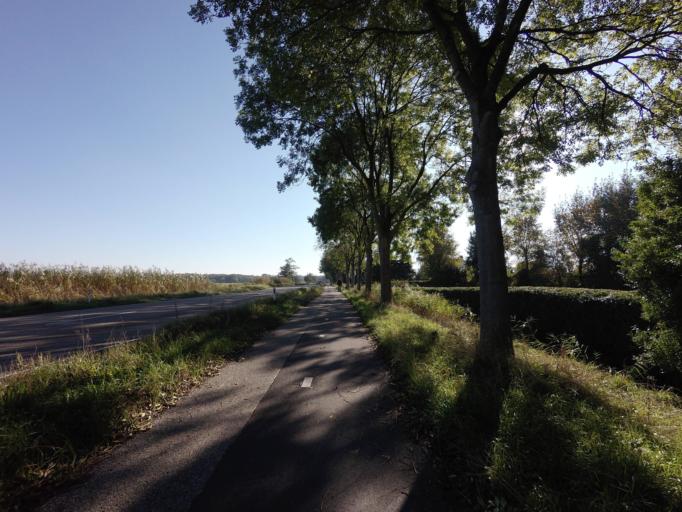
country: NL
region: North Holland
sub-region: Gemeente Wijdemeren
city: Kortenhoef
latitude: 52.2664
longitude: 5.1225
